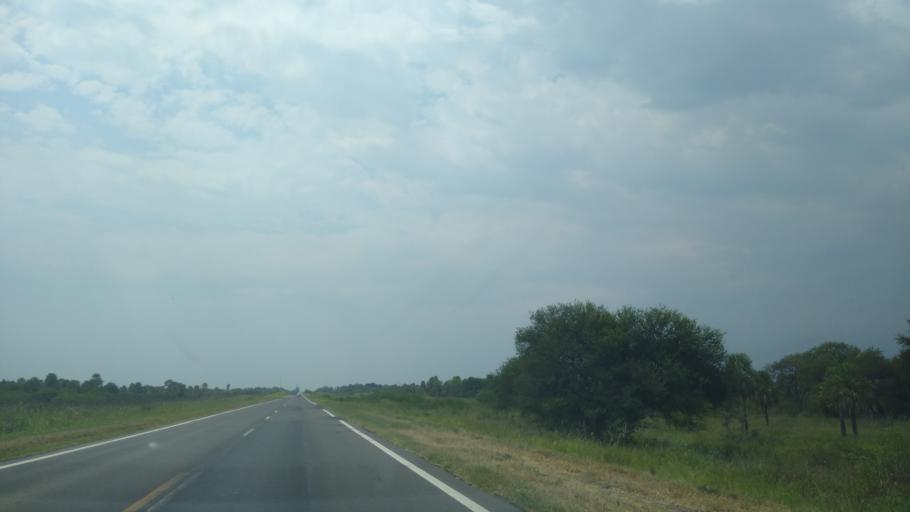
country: AR
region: Chaco
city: Margarita Belen
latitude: -27.1143
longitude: -58.9691
